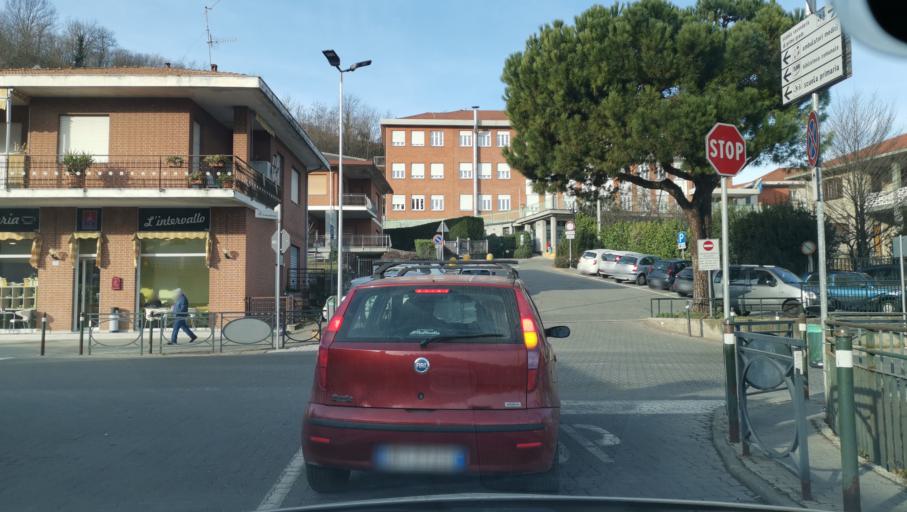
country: IT
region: Piedmont
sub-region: Provincia di Torino
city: Castiglione Torinese
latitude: 45.1205
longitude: 7.8160
